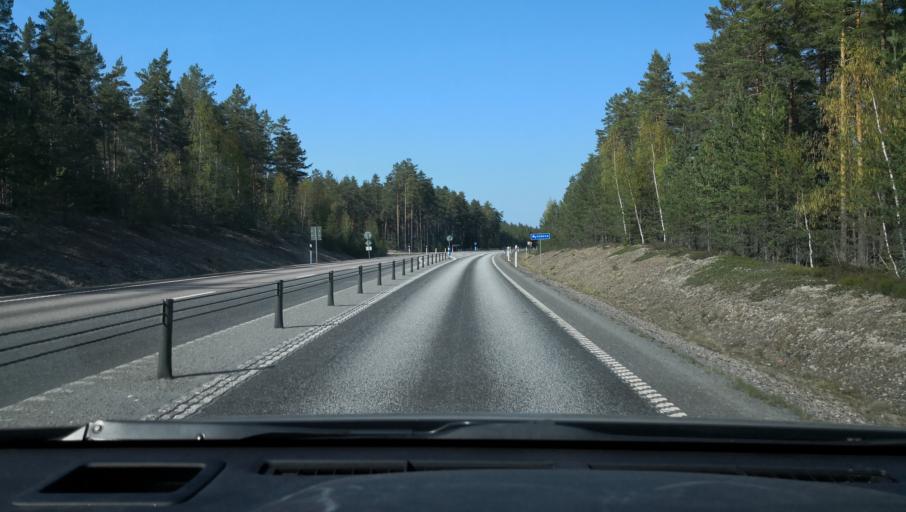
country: SE
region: Uppsala
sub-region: Heby Kommun
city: Tarnsjo
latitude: 60.1897
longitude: 16.9450
